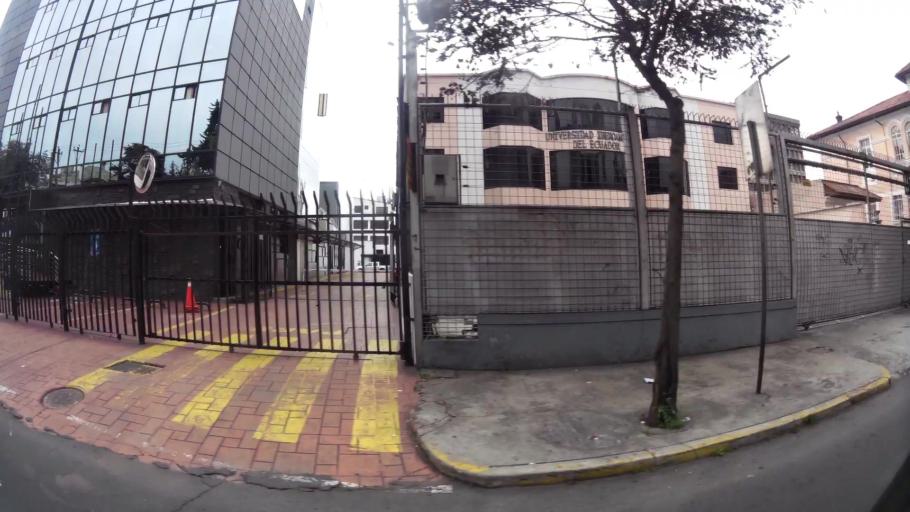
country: EC
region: Pichincha
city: Quito
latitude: -0.1980
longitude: -78.4936
